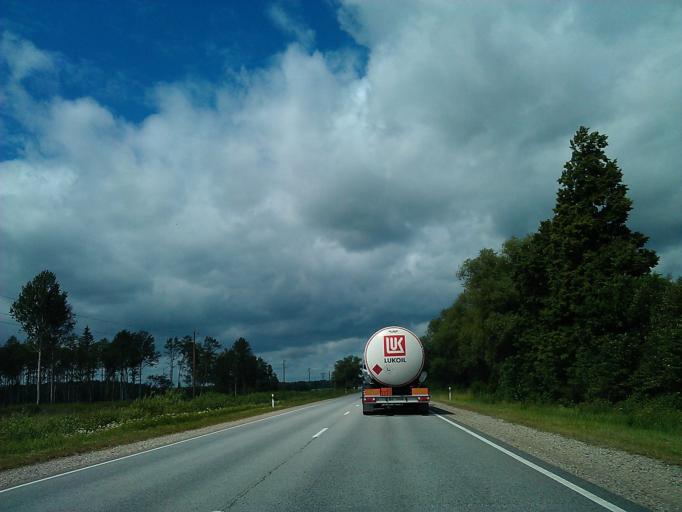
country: LV
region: Engure
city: Smarde
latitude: 56.9133
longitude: 23.3453
